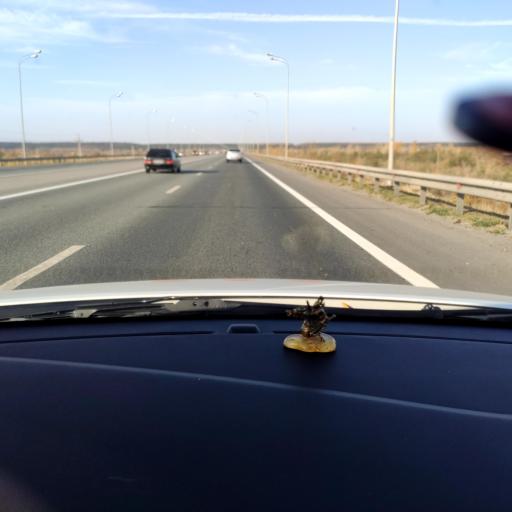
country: RU
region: Tatarstan
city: Osinovo
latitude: 55.8008
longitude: 48.8417
